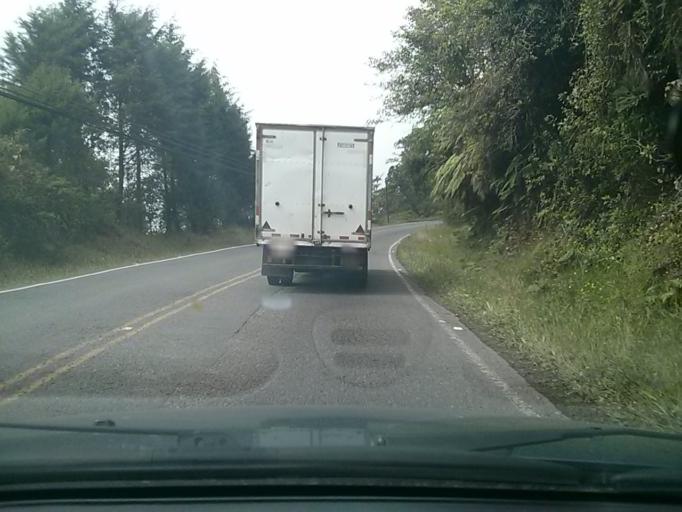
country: CR
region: Cartago
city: Tobosi
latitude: 9.7391
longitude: -83.9510
